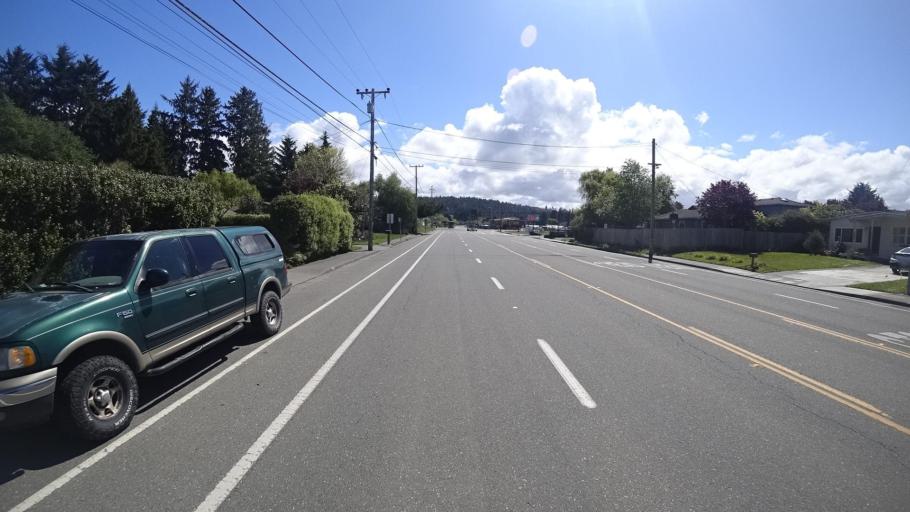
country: US
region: California
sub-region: Humboldt County
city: McKinleyville
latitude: 40.9563
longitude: -124.1024
